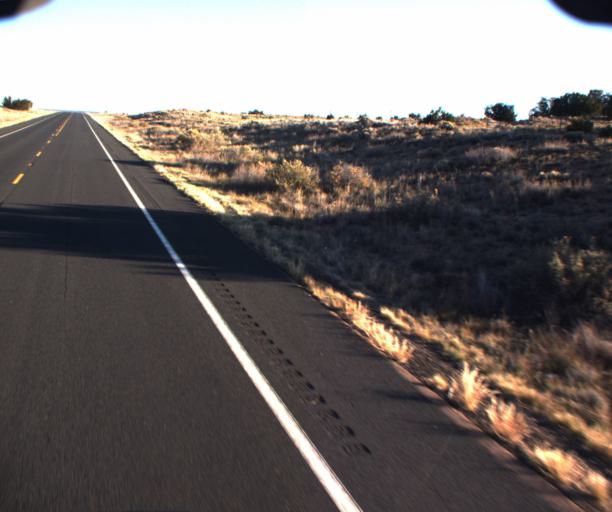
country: US
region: Arizona
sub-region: Apache County
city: Houck
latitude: 35.2836
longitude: -109.4401
